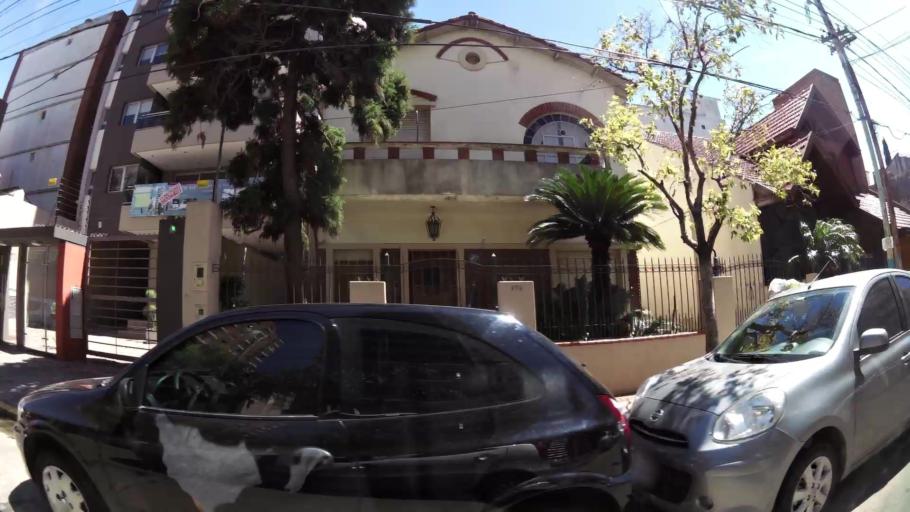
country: AR
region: Buenos Aires
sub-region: Partido de Quilmes
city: Quilmes
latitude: -34.7175
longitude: -58.2589
